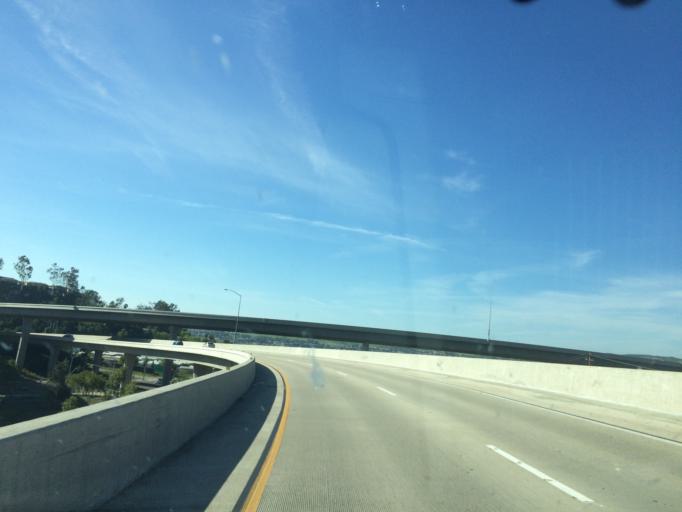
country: US
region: California
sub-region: San Diego County
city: Santee
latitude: 32.8314
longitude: -116.9621
